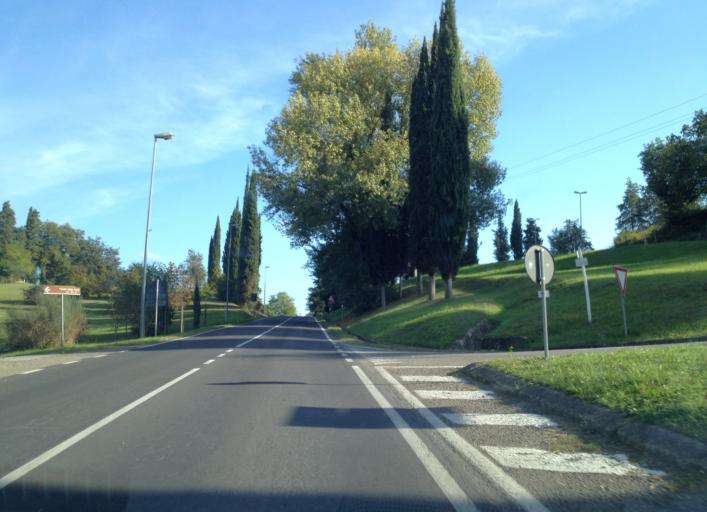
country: IT
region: Tuscany
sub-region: Provincia di Siena
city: Poggibonsi
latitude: 43.4591
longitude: 11.1482
